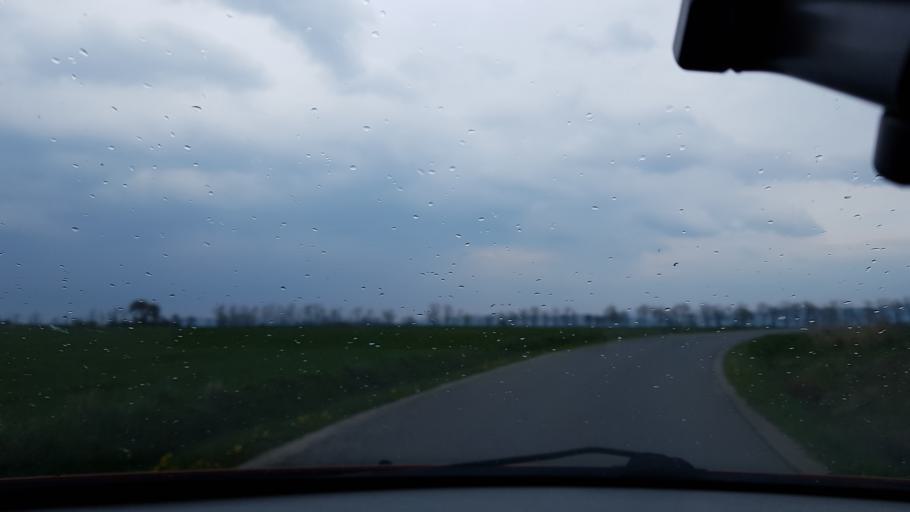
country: PL
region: Lower Silesian Voivodeship
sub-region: Powiat klodzki
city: Bystrzyca Klodzka
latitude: 50.3090
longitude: 16.6134
